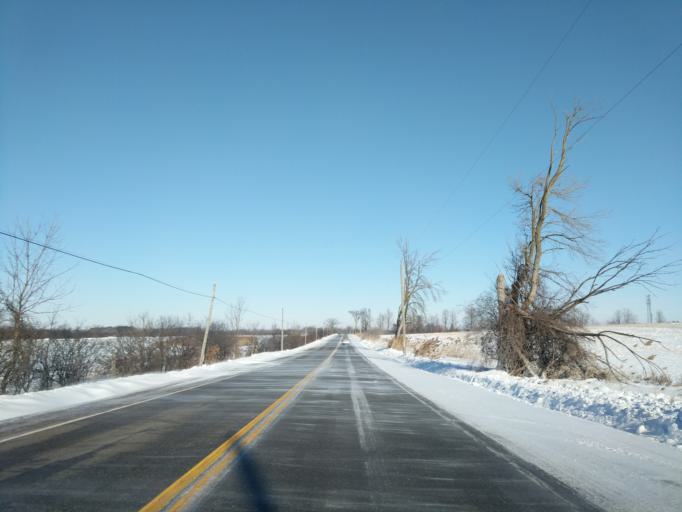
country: CA
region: Ontario
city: Pickering
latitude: 43.8587
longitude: -79.1325
